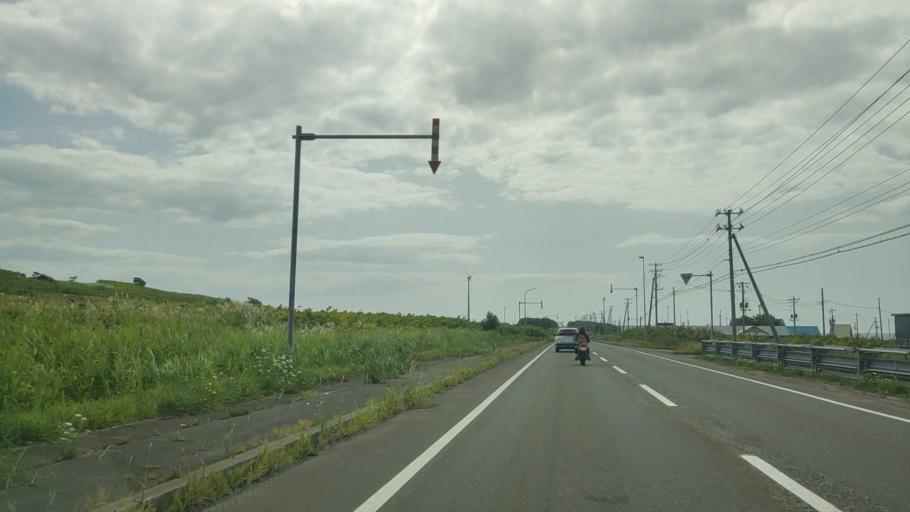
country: JP
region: Hokkaido
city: Rumoi
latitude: 44.4029
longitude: 141.7263
